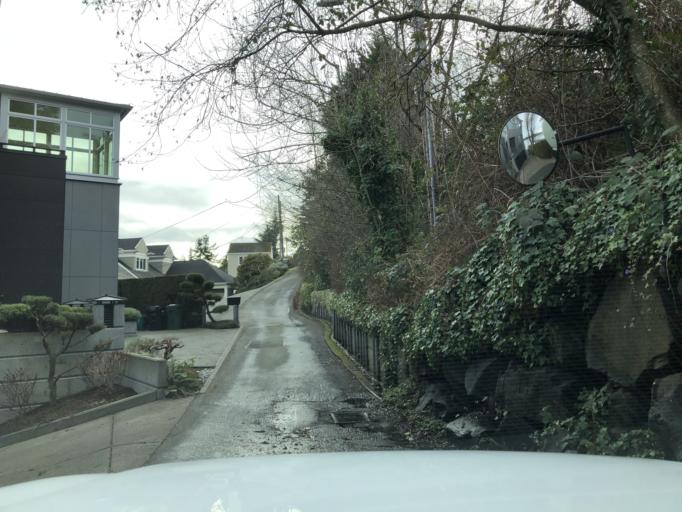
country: US
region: Washington
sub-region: King County
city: Inglewood-Finn Hill
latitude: 47.7035
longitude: -122.2744
